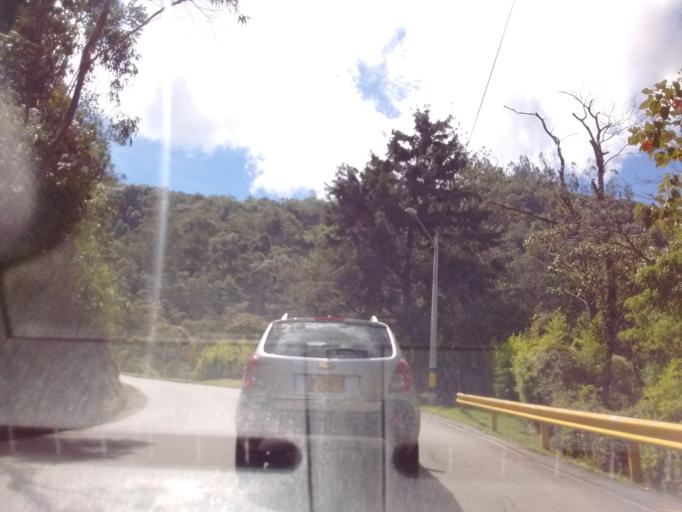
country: CO
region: Antioquia
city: Medellin
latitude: 6.2326
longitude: -75.5071
